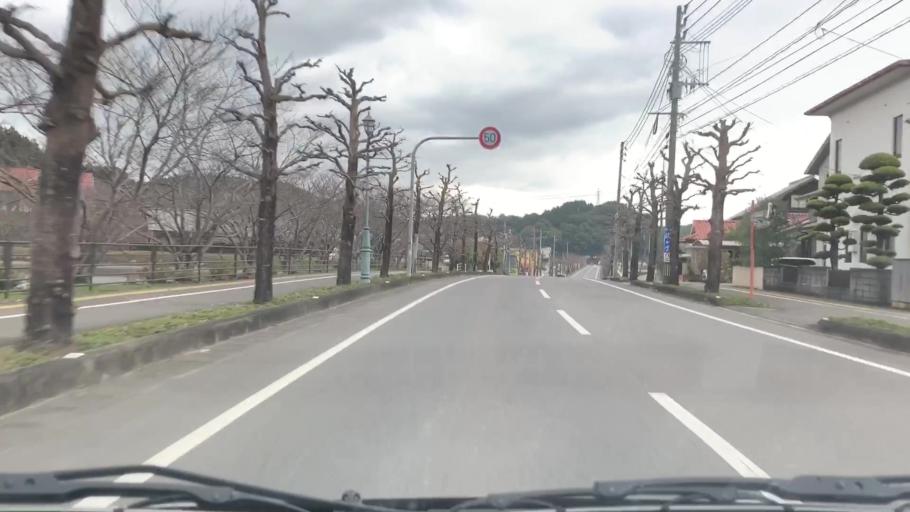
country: JP
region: Saga Prefecture
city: Ureshinomachi-shimojuku
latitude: 33.1031
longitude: 129.9859
